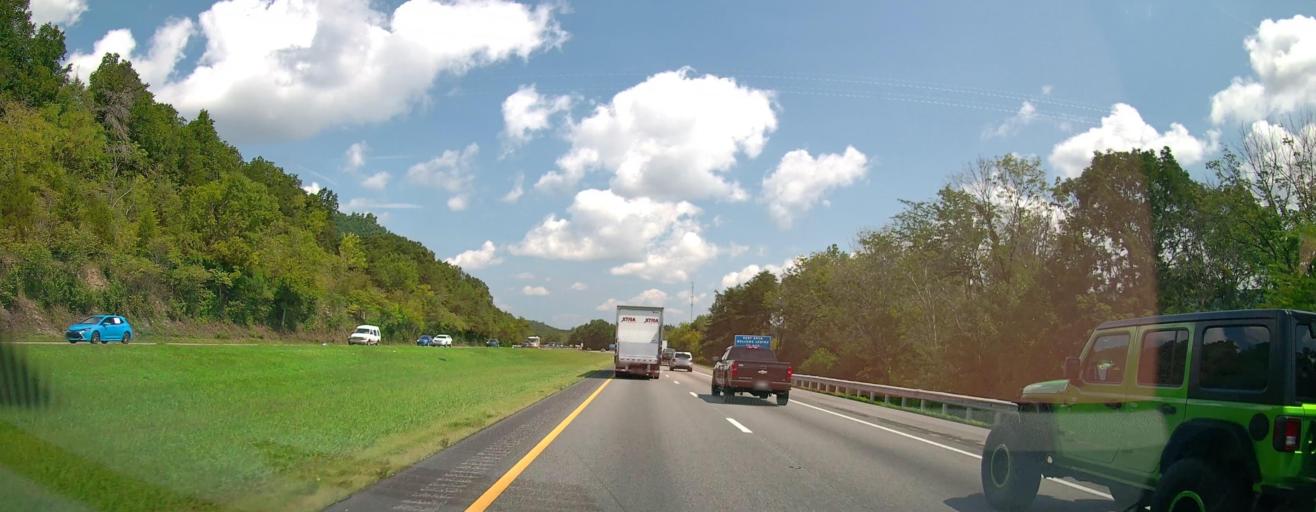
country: US
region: Georgia
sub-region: Walker County
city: Lookout Mountain
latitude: 34.9852
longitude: -85.4061
